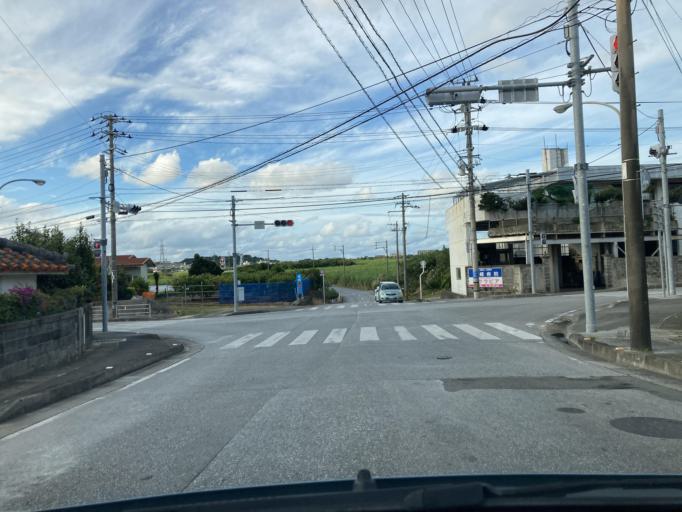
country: JP
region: Okinawa
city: Itoman
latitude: 26.1369
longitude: 127.6984
